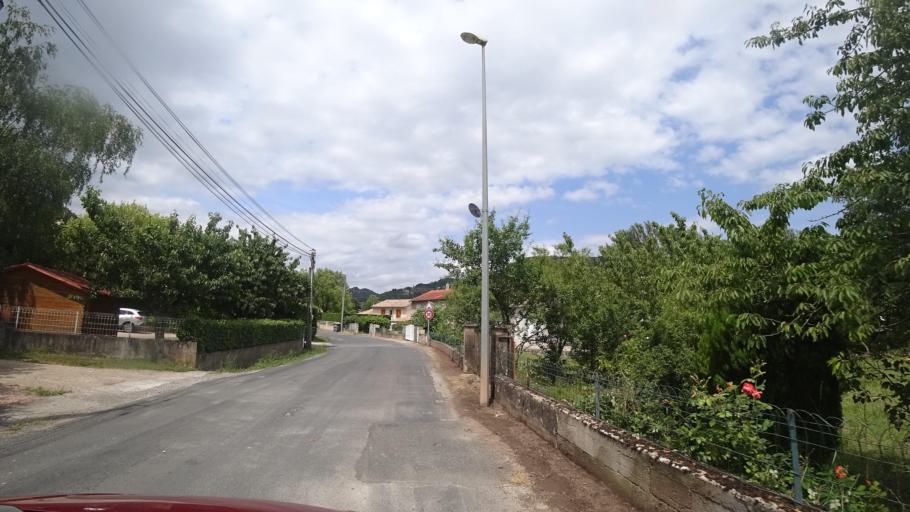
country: FR
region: Midi-Pyrenees
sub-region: Departement de l'Aveyron
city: Saint-Affrique
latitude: 43.9470
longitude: 2.8921
